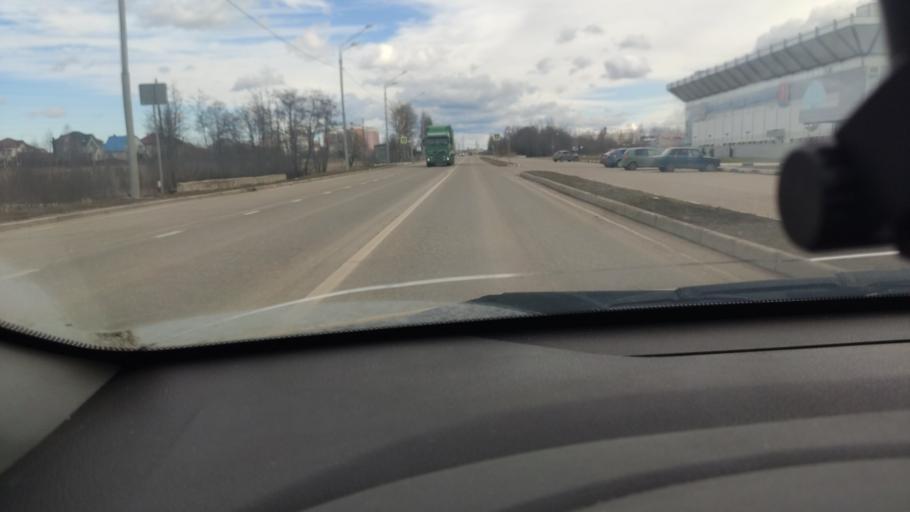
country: RU
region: Moskovskaya
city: Ruza
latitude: 55.7090
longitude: 36.1902
